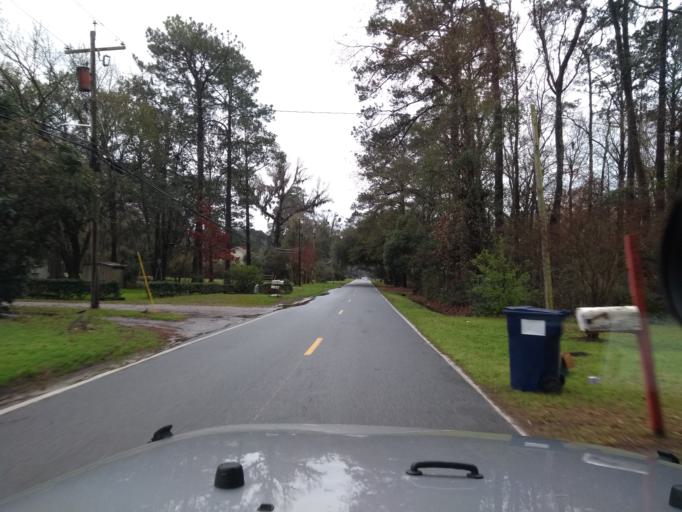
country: US
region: Georgia
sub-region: Chatham County
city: Savannah
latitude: 32.0312
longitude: -81.1601
